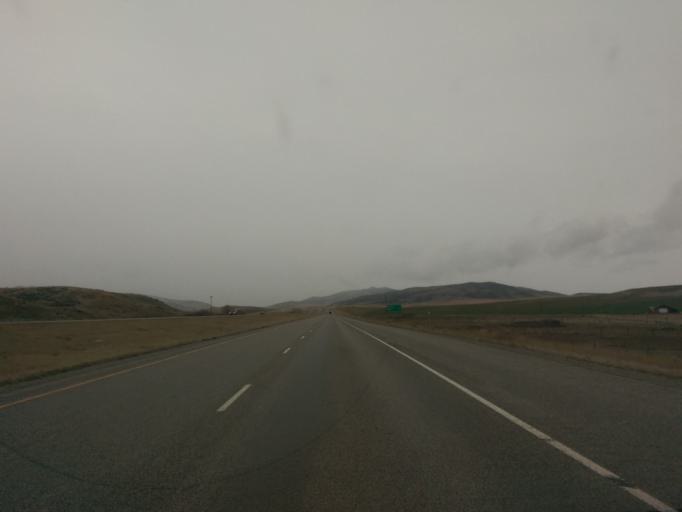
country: US
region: Montana
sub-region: Gallatin County
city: Three Forks
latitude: 45.9142
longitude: -111.7586
